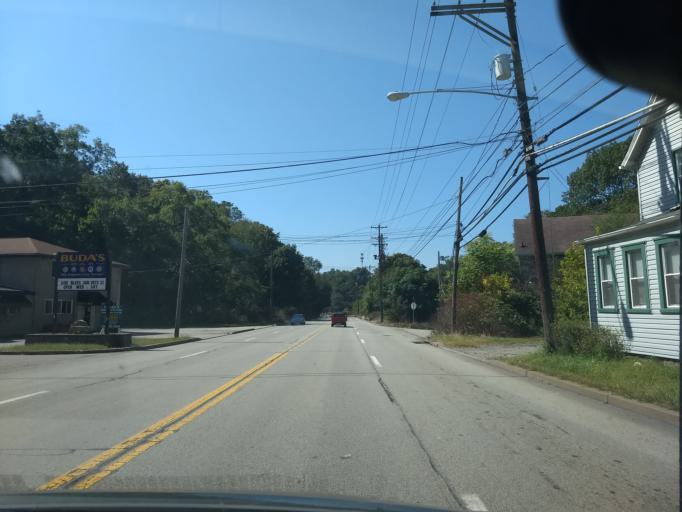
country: US
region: Pennsylvania
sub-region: Allegheny County
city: North Versailles
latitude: 40.3616
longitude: -79.8271
